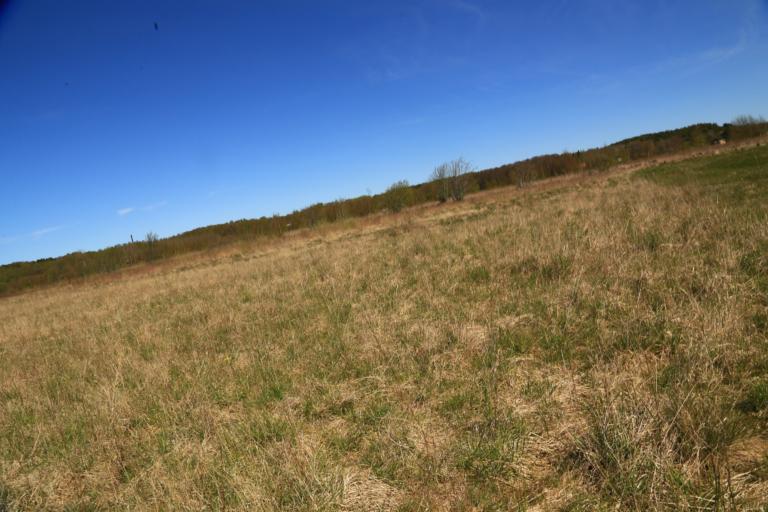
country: SE
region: Halland
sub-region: Varbergs Kommun
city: Traslovslage
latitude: 57.0870
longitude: 12.2840
